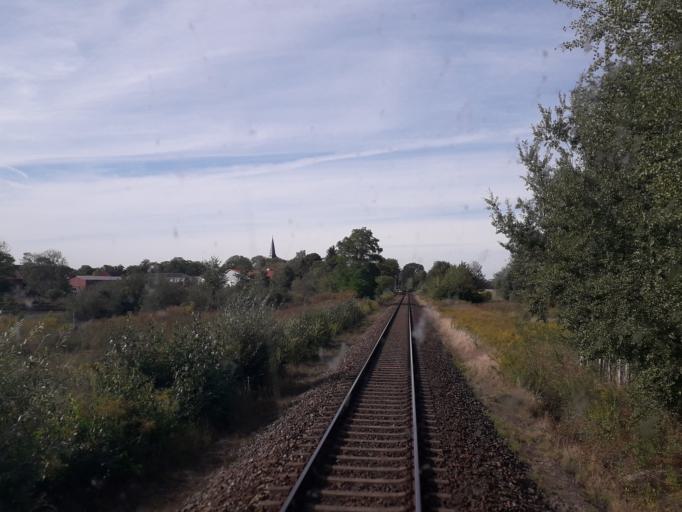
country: DE
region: Brandenburg
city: Kremmen
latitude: 52.7330
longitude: 13.0950
